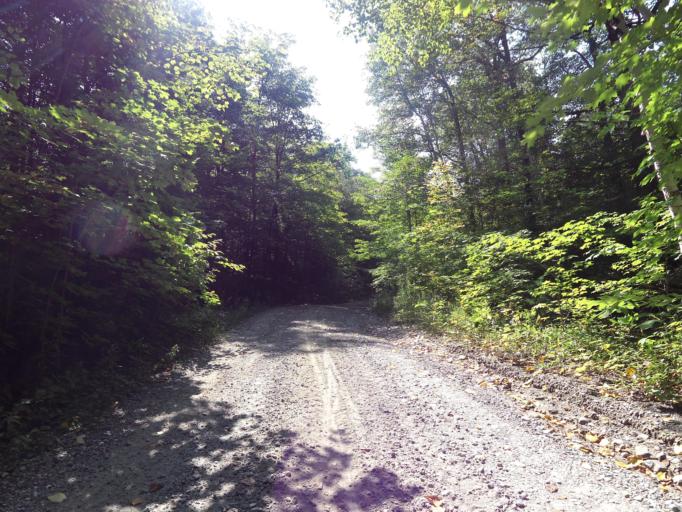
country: CA
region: Ontario
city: Perth
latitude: 45.0252
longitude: -76.6223
